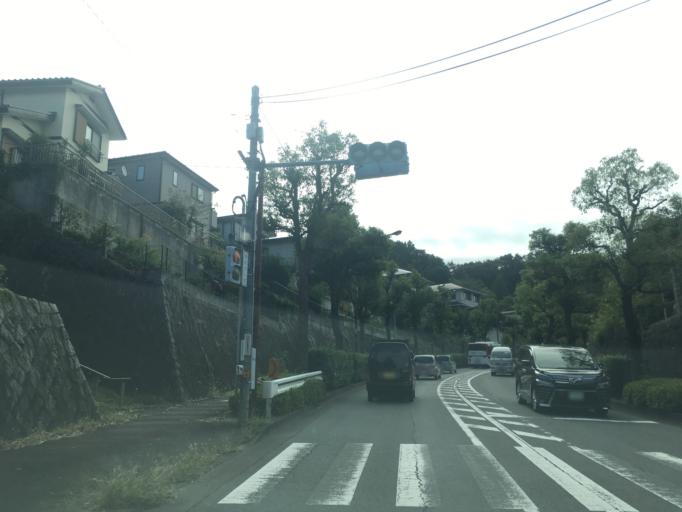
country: JP
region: Tokyo
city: Hino
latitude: 35.6438
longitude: 139.3872
